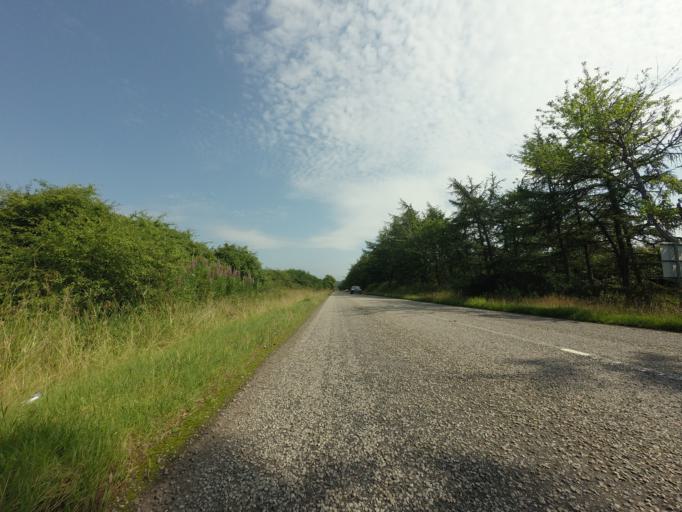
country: GB
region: Scotland
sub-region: Highland
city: Evanton
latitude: 57.9161
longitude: -4.3890
